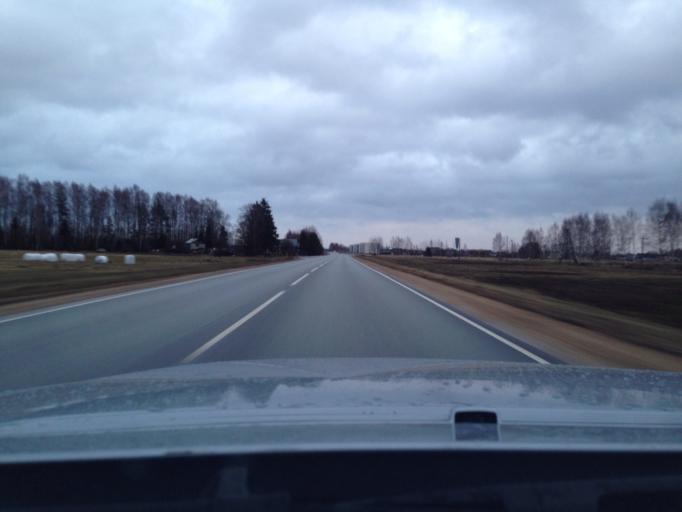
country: LV
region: Marupe
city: Marupe
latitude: 56.8935
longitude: 24.0172
